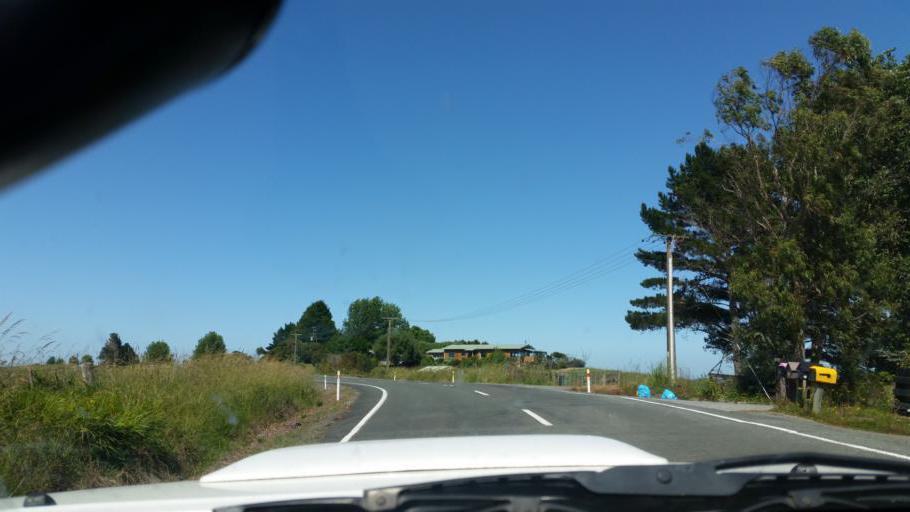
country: NZ
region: Auckland
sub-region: Auckland
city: Wellsford
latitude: -36.2189
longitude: 174.3828
